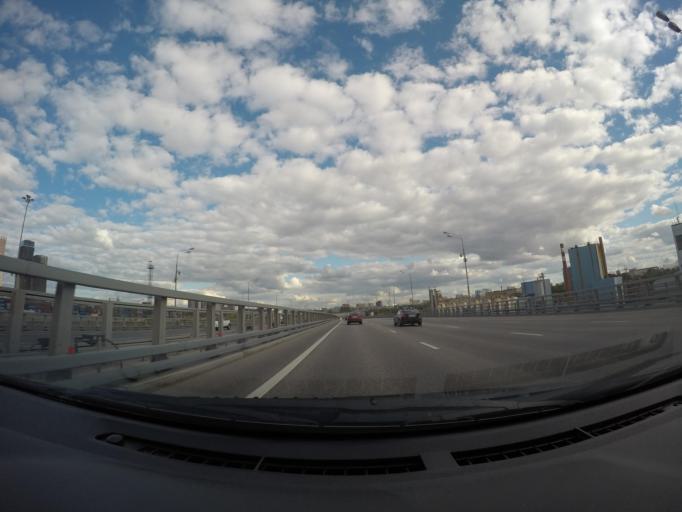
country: RU
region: Moscow
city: Zapadnoye Degunino
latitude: 55.8571
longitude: 37.5349
